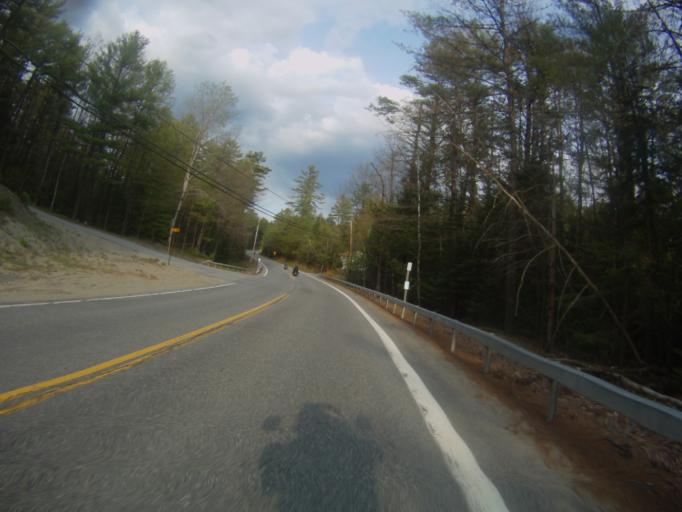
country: US
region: New York
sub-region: Warren County
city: Warrensburg
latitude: 43.6628
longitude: -73.8548
